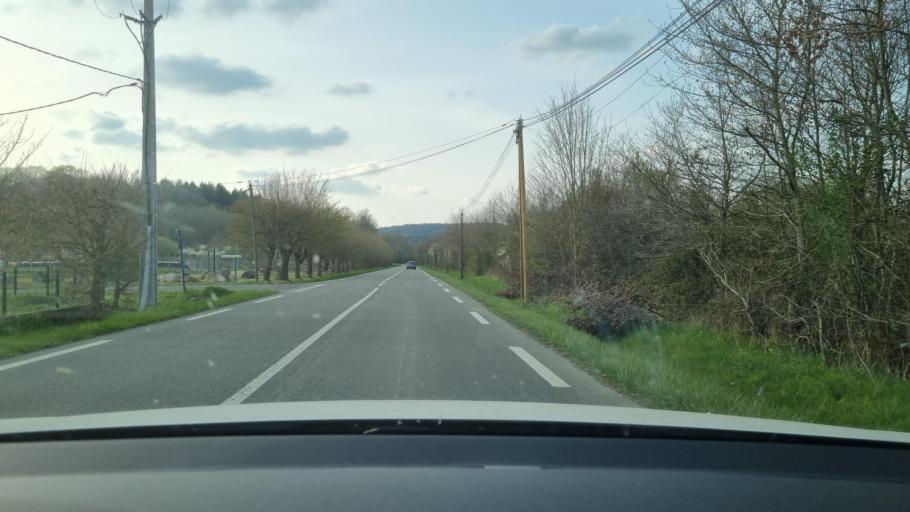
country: FR
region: Midi-Pyrenees
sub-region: Departement des Hautes-Pyrenees
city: Vic-en-Bigorre
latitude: 43.3906
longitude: 0.0306
